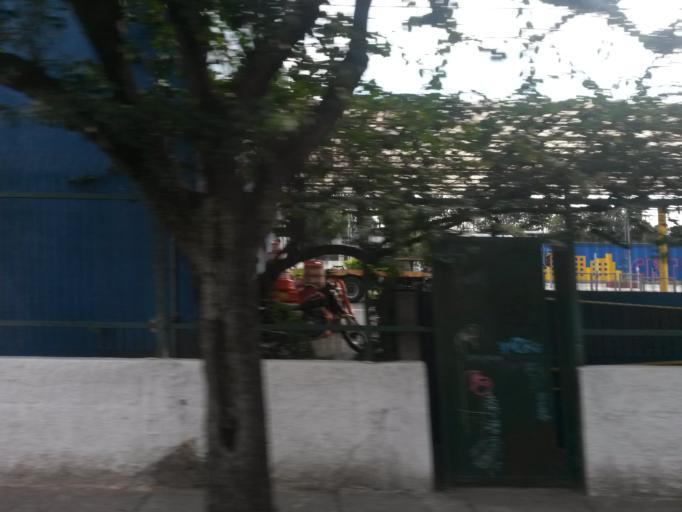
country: BR
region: Sao Paulo
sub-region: Sao Bernardo Do Campo
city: Sao Bernardo do Campo
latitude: -23.6779
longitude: -46.5573
